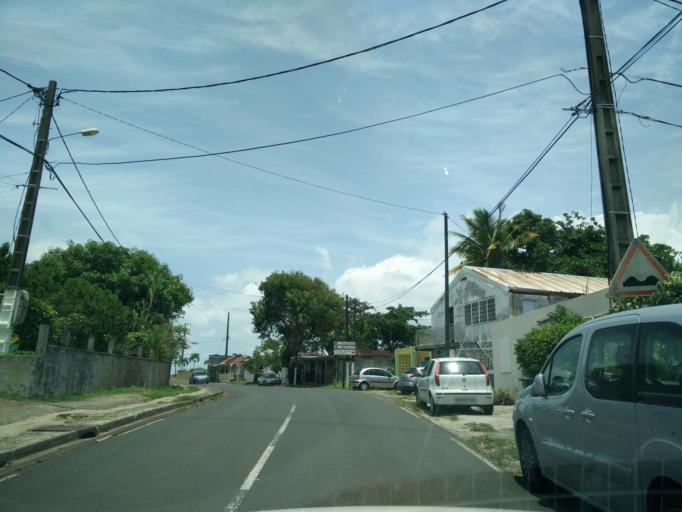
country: GP
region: Guadeloupe
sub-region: Guadeloupe
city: Petit-Bourg
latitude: 16.1873
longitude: -61.5899
